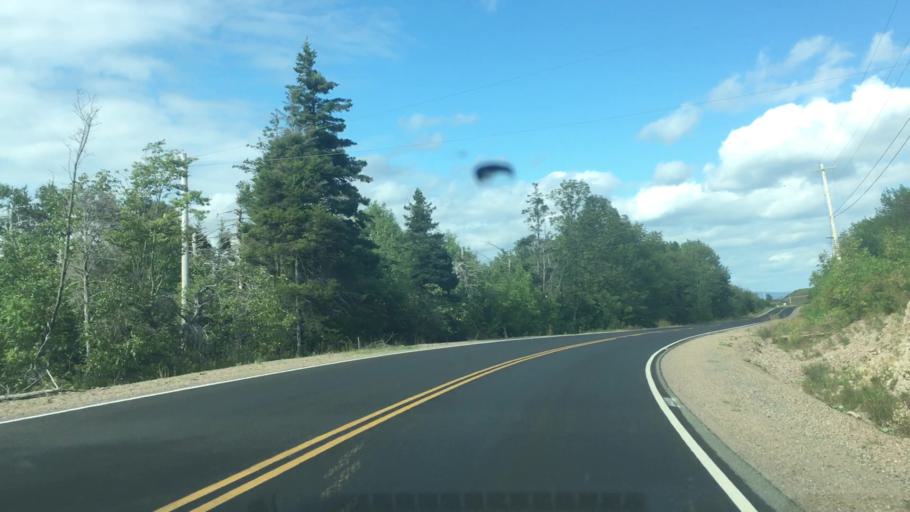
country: CA
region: Nova Scotia
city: Princeville
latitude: 45.7948
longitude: -60.7368
